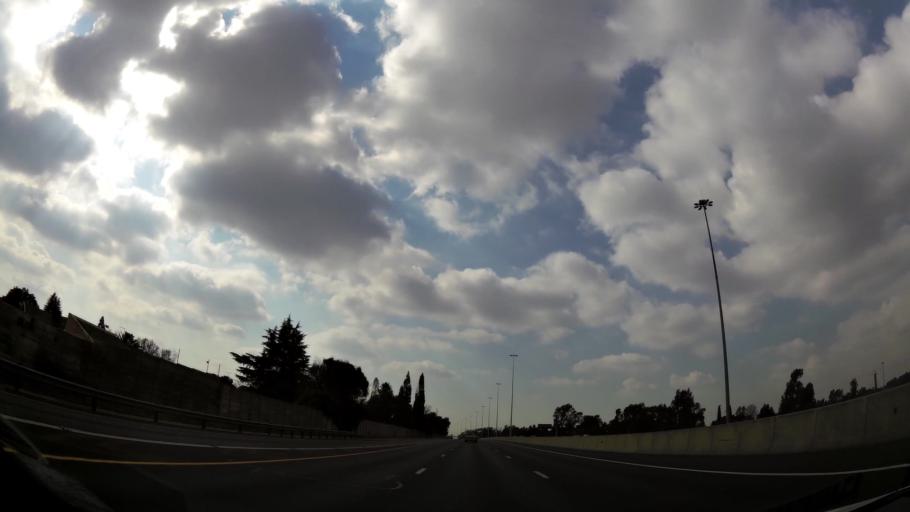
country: ZA
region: Gauteng
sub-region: Ekurhuleni Metropolitan Municipality
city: Benoni
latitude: -26.1747
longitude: 28.3370
